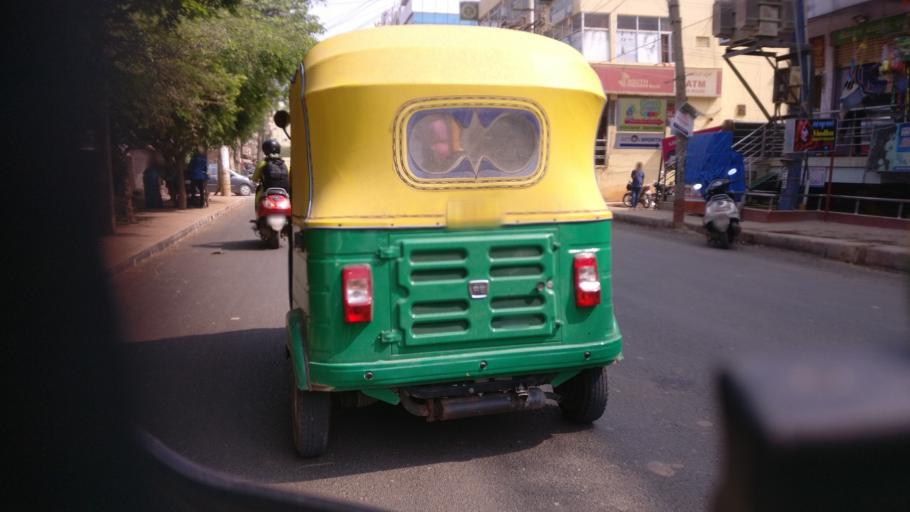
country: IN
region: Karnataka
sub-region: Bangalore Urban
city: Bangalore
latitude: 12.9038
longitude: 77.6759
